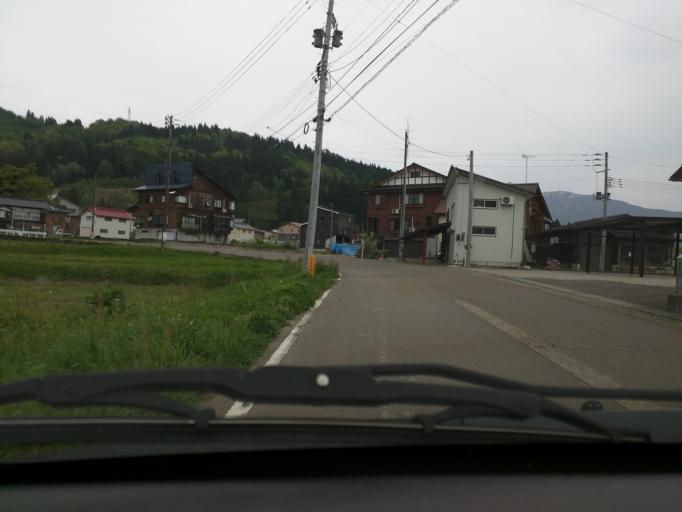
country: JP
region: Niigata
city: Muikamachi
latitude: 37.1935
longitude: 138.9524
